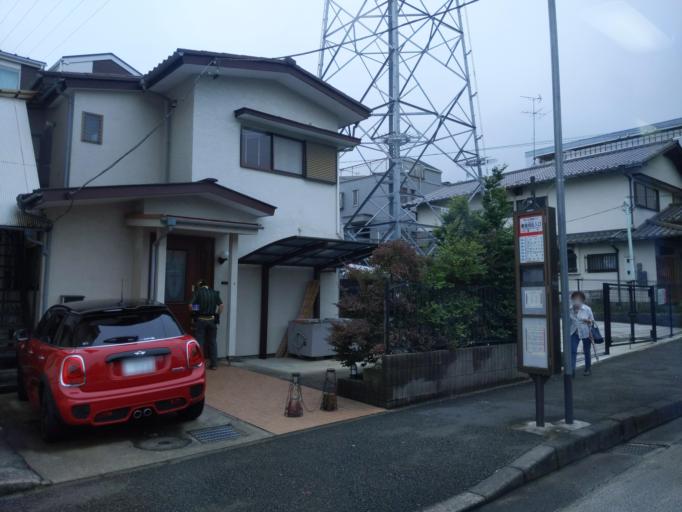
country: JP
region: Tokyo
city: Chofugaoka
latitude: 35.5947
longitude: 139.5711
